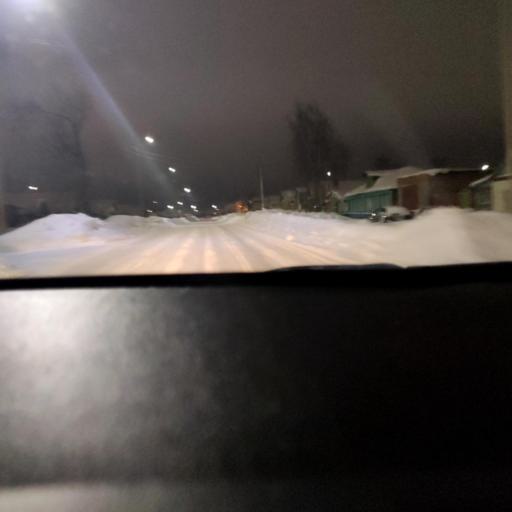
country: RU
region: Tatarstan
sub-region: Chistopol'skiy Rayon
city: Chistopol'
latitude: 55.3601
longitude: 50.6283
